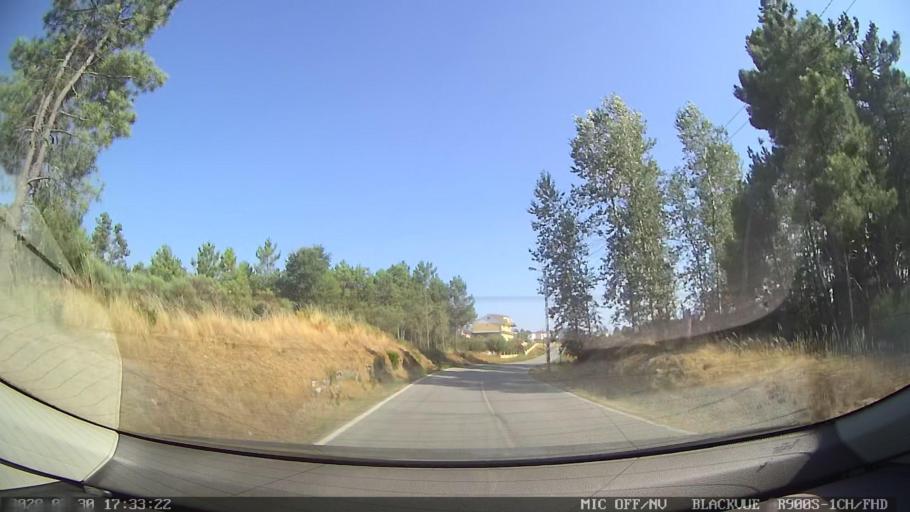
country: PT
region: Vila Real
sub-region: Murca
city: Murca
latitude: 41.3501
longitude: -7.4742
